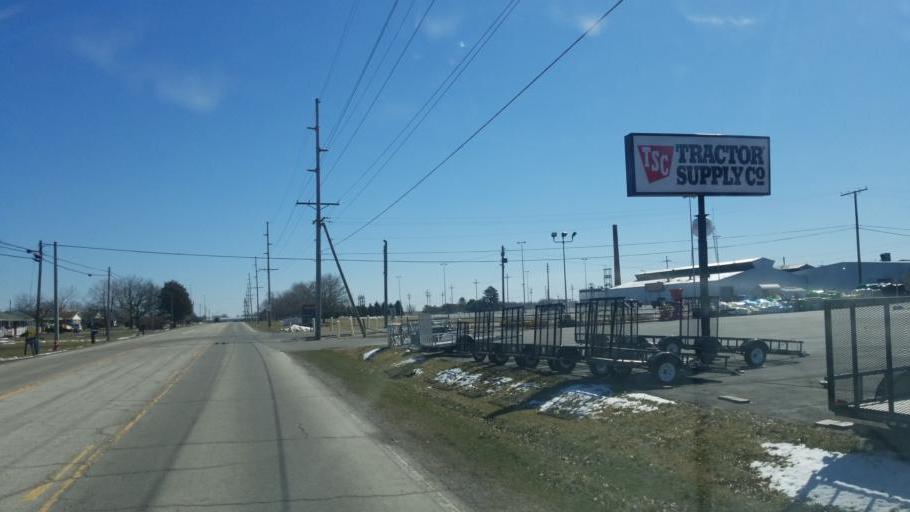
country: US
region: Ohio
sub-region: Crawford County
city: Bucyrus
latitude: 40.8125
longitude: -82.9432
